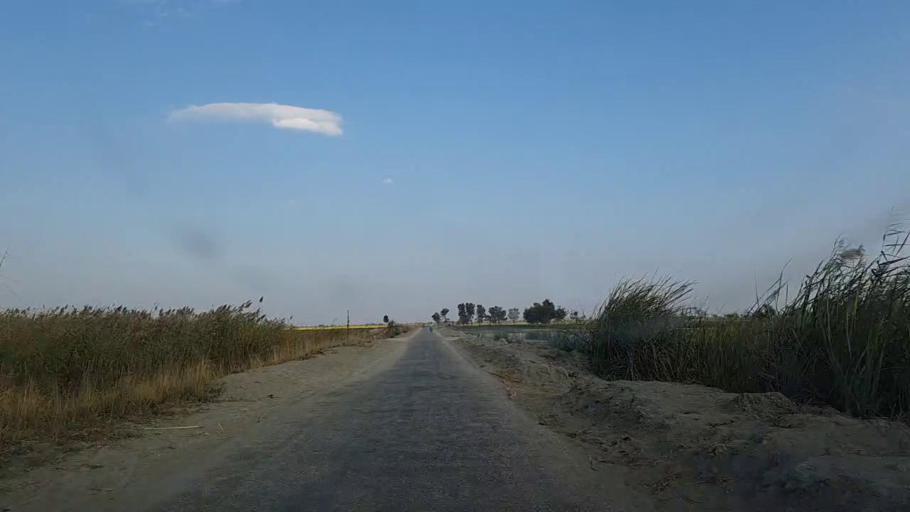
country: PK
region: Sindh
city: Sanghar
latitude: 26.2644
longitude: 68.9349
